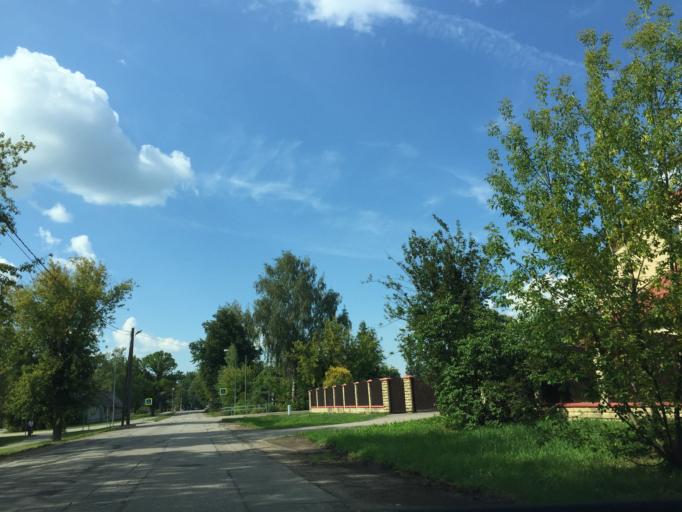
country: LV
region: Sigulda
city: Sigulda
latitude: 57.1521
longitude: 24.8610
